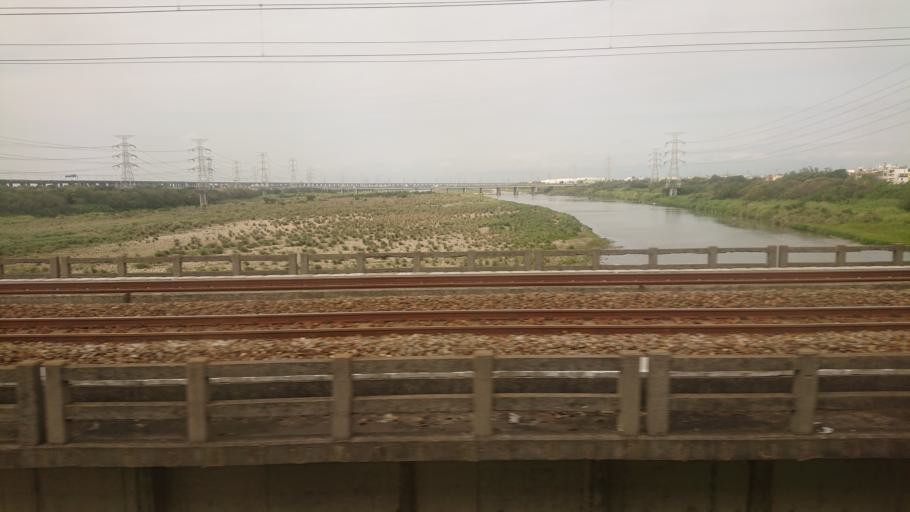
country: TW
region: Taiwan
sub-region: Changhua
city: Chang-hua
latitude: 24.1078
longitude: 120.5774
